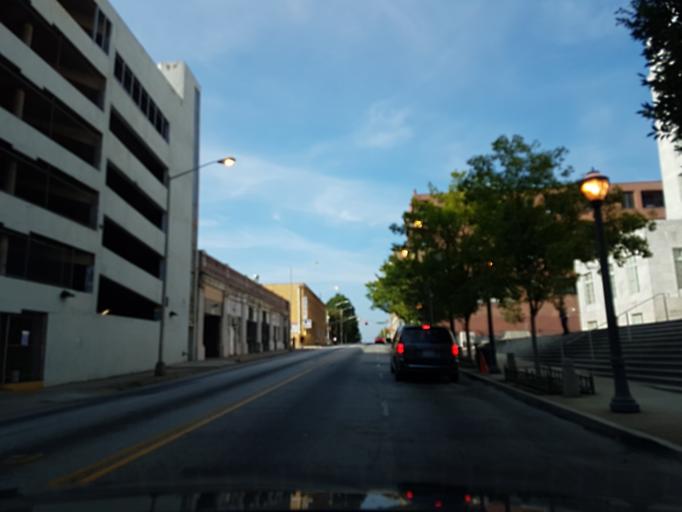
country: US
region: Georgia
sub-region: Fulton County
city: Atlanta
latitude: 33.7527
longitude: -84.3936
